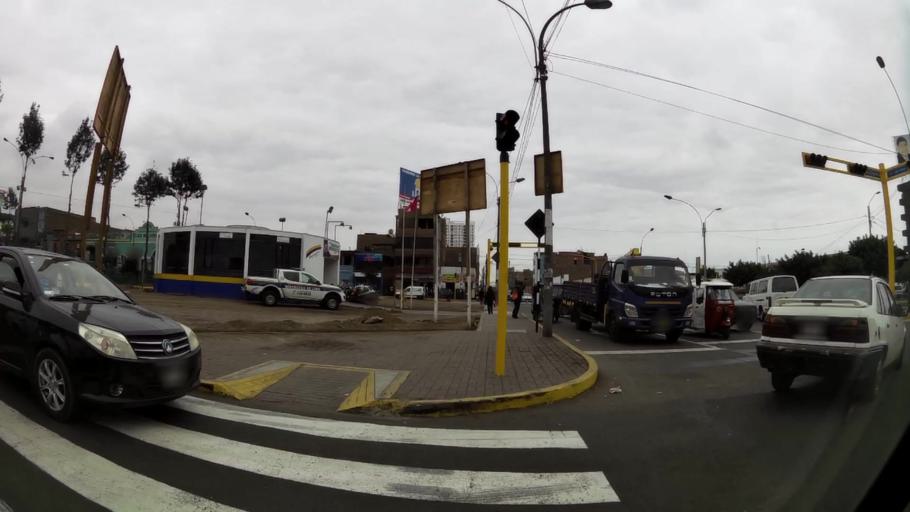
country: PE
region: Lima
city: Lima
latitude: -12.0439
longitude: -77.0510
